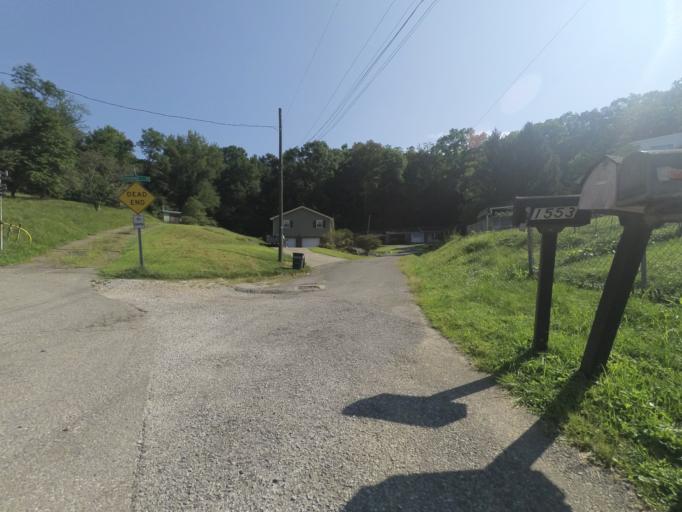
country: US
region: West Virginia
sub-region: Cabell County
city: Huntington
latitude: 38.4000
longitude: -82.4616
